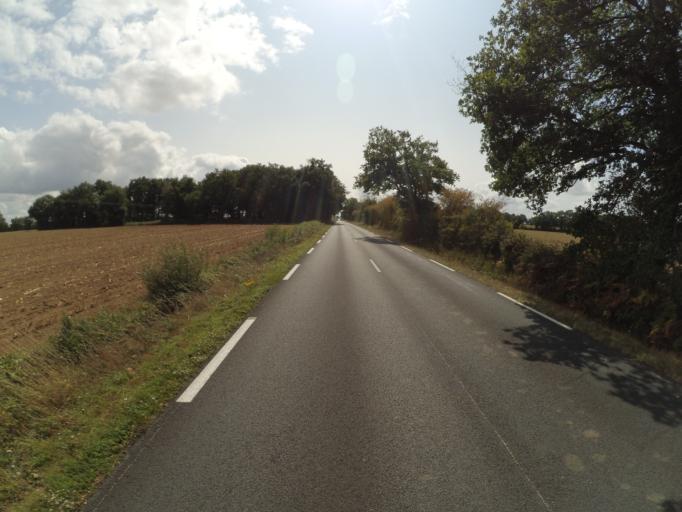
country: FR
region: Pays de la Loire
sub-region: Departement de la Vendee
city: La Bernardiere
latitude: 47.0115
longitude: -1.2794
